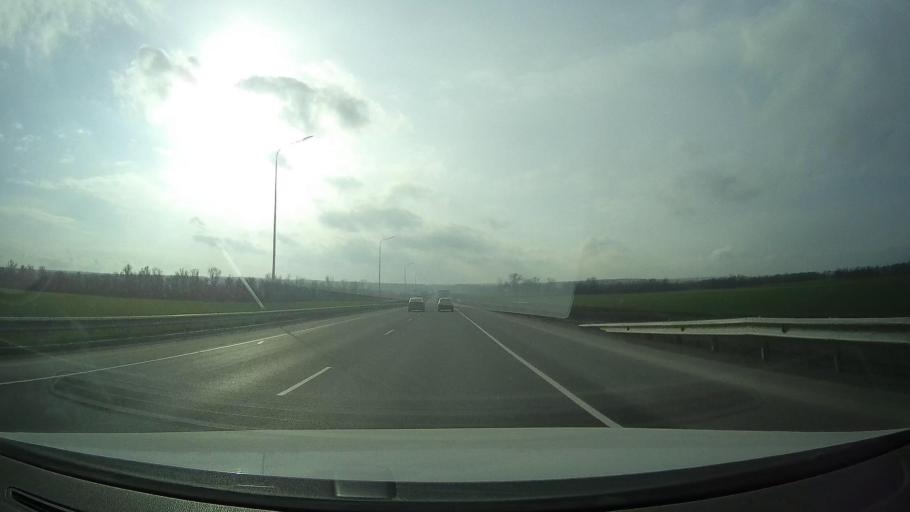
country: RU
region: Rostov
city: Grushevskaya
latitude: 47.4530
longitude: 39.8823
